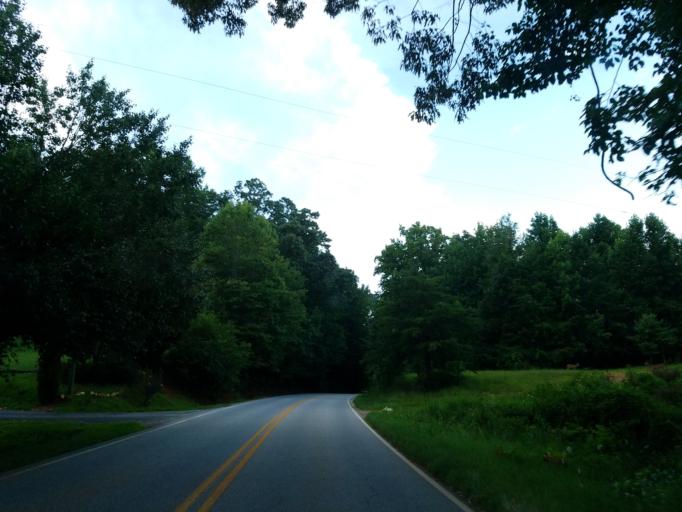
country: US
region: Georgia
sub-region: Lumpkin County
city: Dahlonega
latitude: 34.5919
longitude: -83.9694
